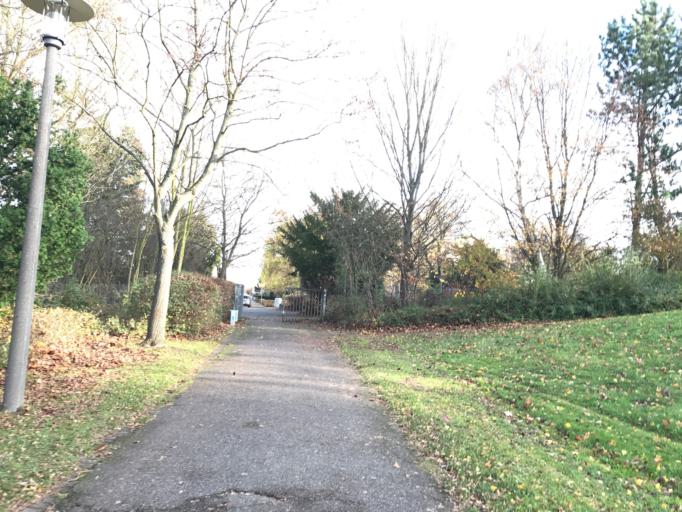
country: DE
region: North Rhine-Westphalia
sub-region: Regierungsbezirk Koln
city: Rheinbach
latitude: 50.6207
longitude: 6.9364
